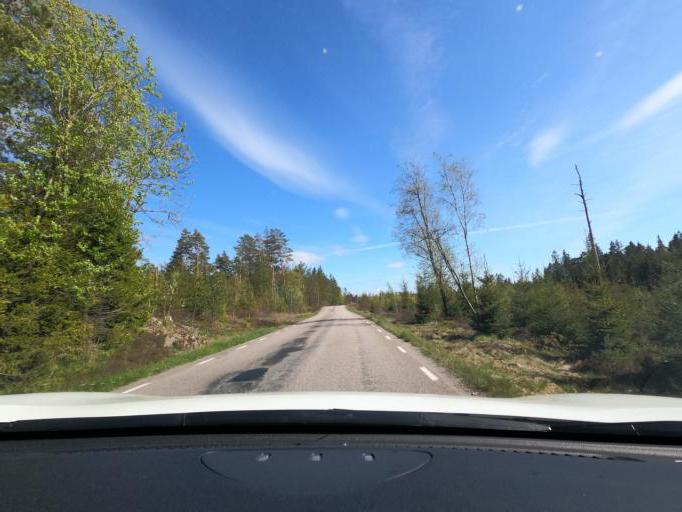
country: SE
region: Vaestra Goetaland
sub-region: Harryda Kommun
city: Hindas
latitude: 57.6615
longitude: 12.3547
